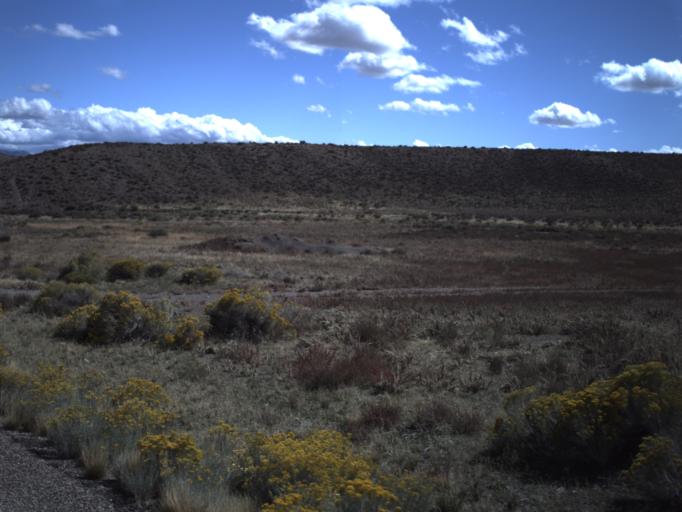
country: US
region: Utah
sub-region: Beaver County
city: Milford
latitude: 38.4394
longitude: -113.1554
